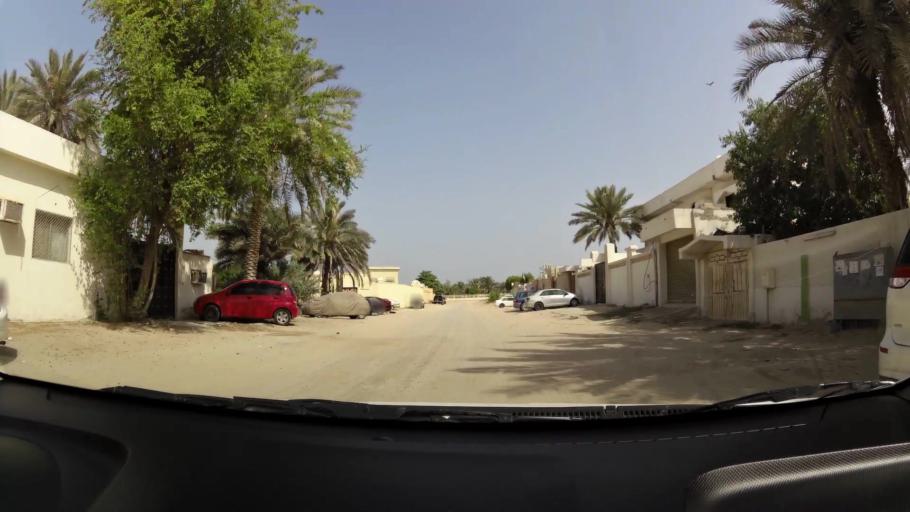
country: AE
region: Ash Shariqah
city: Sharjah
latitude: 25.3474
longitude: 55.4158
